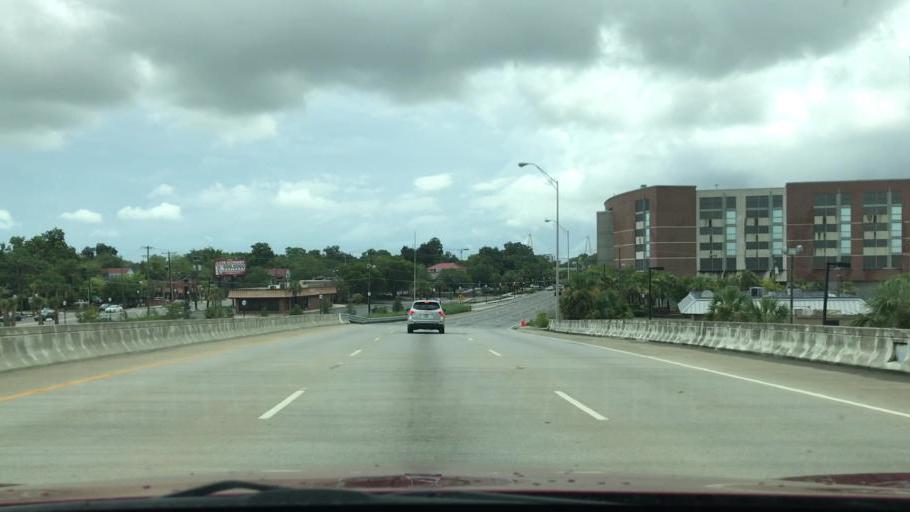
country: US
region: South Carolina
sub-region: Charleston County
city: Charleston
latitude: 32.7856
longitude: -79.9554
